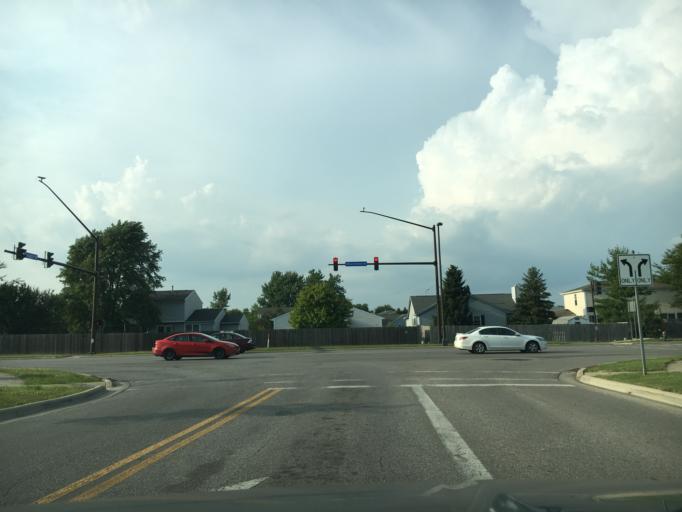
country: US
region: Ohio
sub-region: Franklin County
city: Hilliard
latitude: 40.0166
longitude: -83.1568
